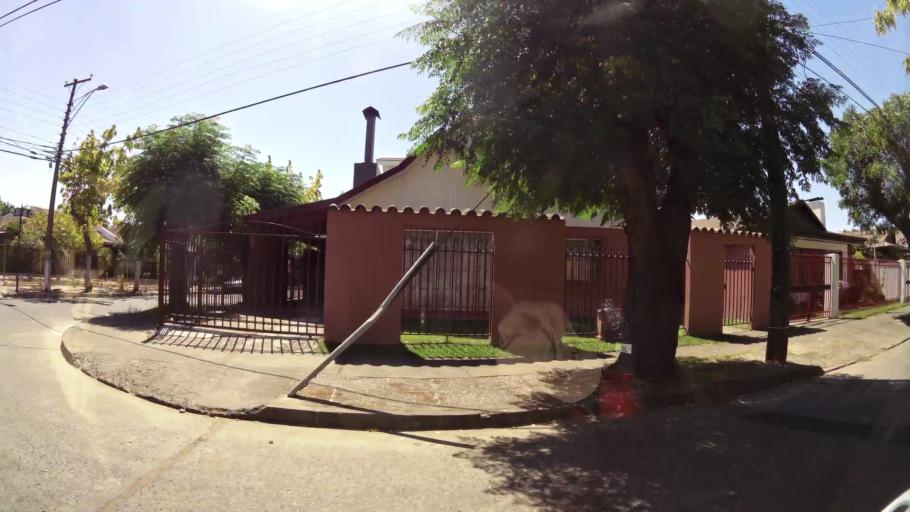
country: CL
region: Maule
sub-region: Provincia de Talca
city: Talca
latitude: -35.4147
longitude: -71.6556
